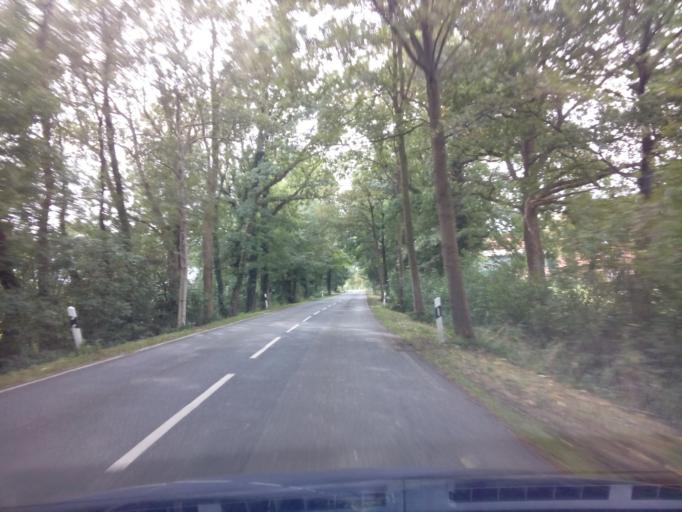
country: DE
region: Lower Saxony
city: Kohlen
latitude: 53.4851
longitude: 8.8602
